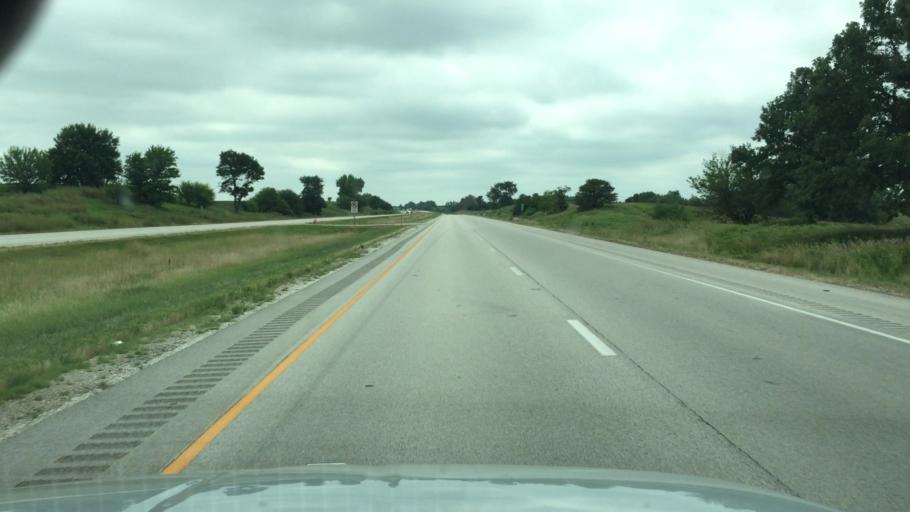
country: US
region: Illinois
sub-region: Henry County
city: Orion
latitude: 41.3389
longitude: -90.3337
